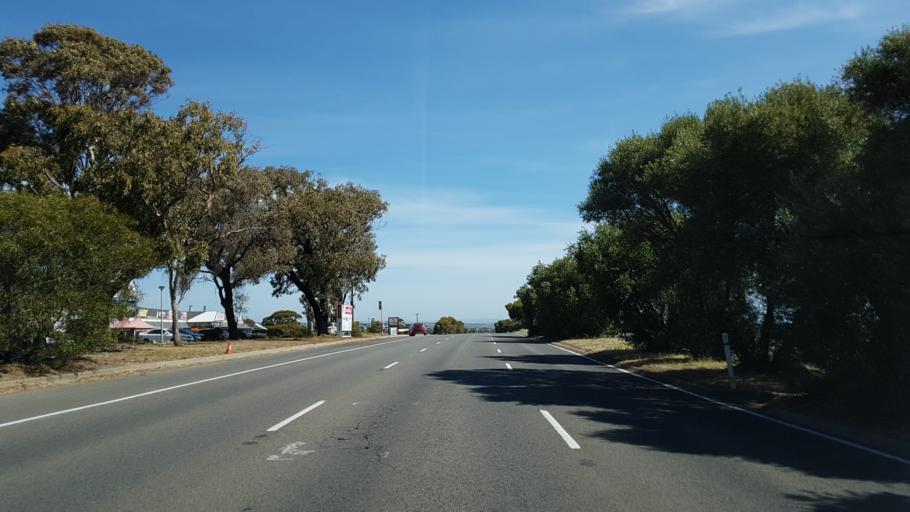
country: AU
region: South Australia
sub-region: Marion
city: Trott Park
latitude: -35.0671
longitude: 138.5550
